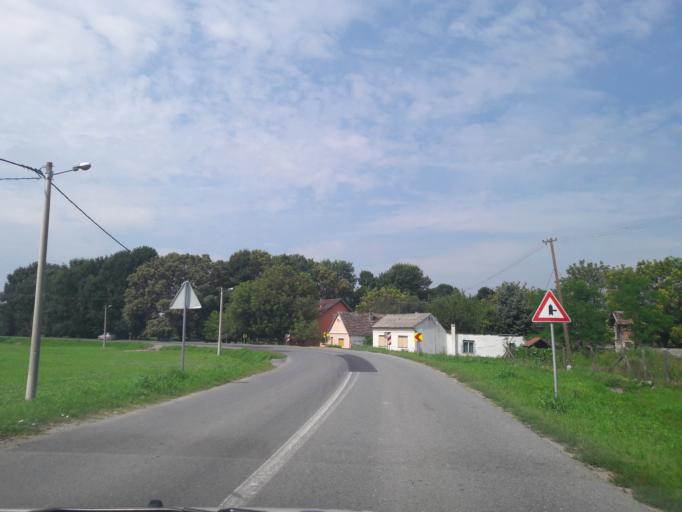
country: HR
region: Osjecko-Baranjska
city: Bizovac
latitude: 45.5147
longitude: 18.4736
